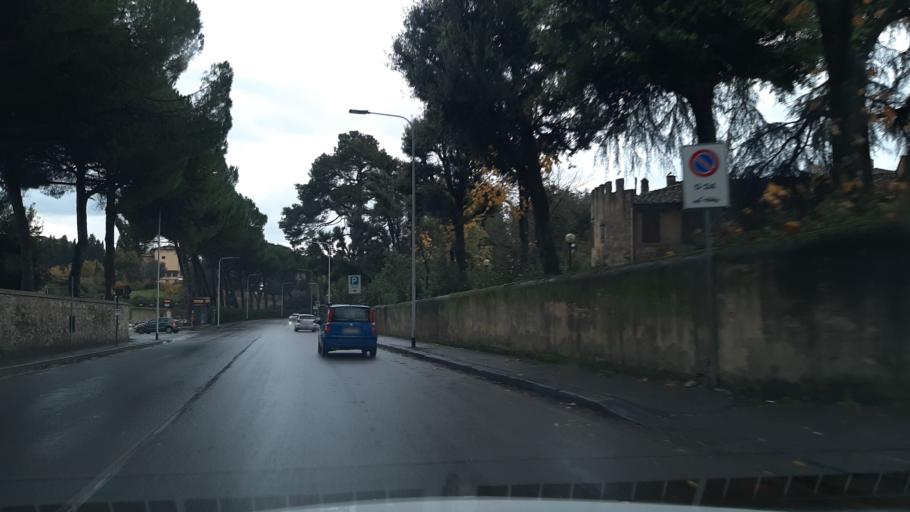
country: IT
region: Tuscany
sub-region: Province of Florence
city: Florence
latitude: 43.8103
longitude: 11.2500
